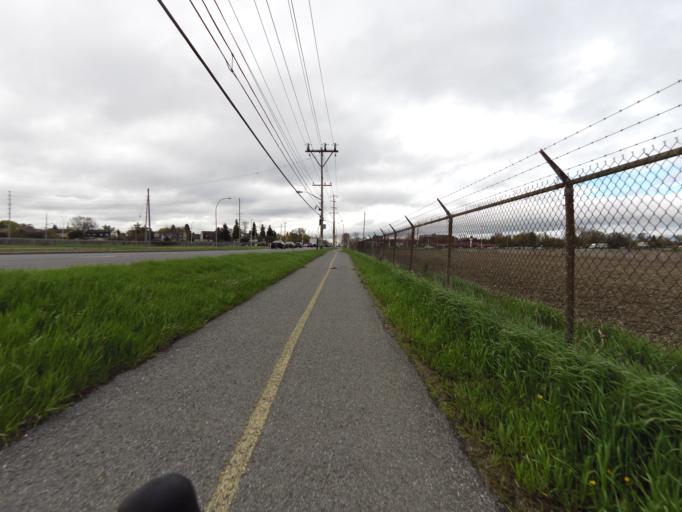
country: CA
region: Ontario
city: Bells Corners
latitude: 45.2895
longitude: -75.7581
